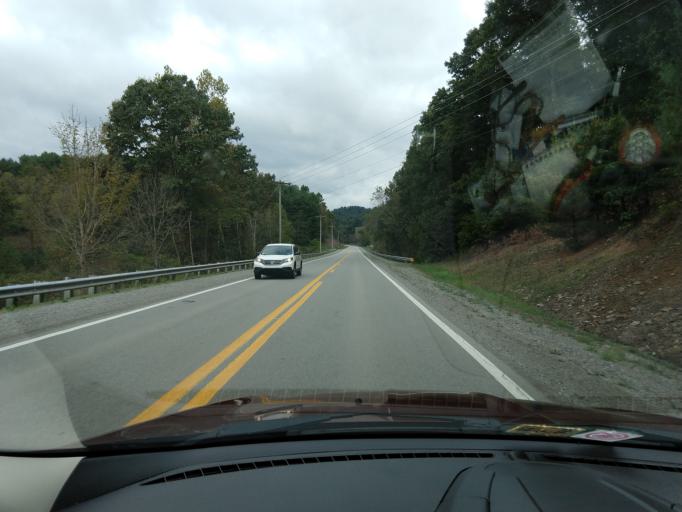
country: US
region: West Virginia
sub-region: Barbour County
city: Belington
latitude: 39.0380
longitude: -79.9552
